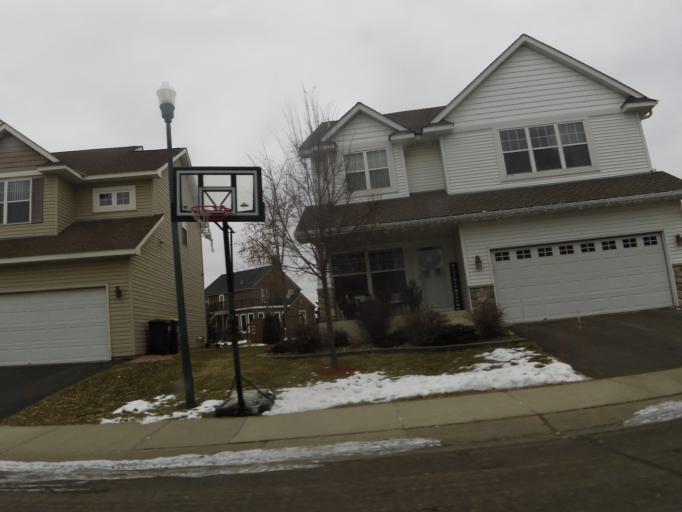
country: US
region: Minnesota
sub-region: Carver County
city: Chaska
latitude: 44.8068
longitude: -93.6168
